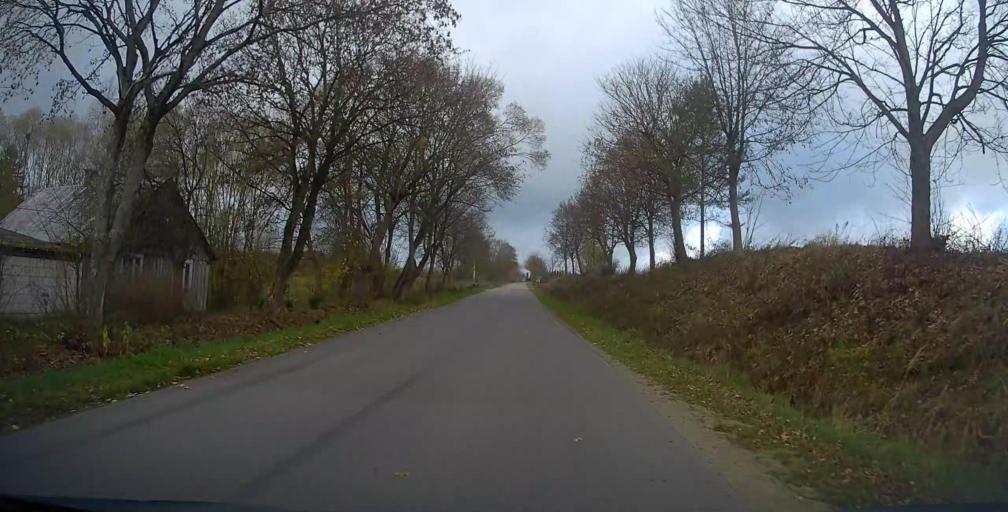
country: PL
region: Podlasie
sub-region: Suwalki
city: Suwalki
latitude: 54.3112
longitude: 22.8806
